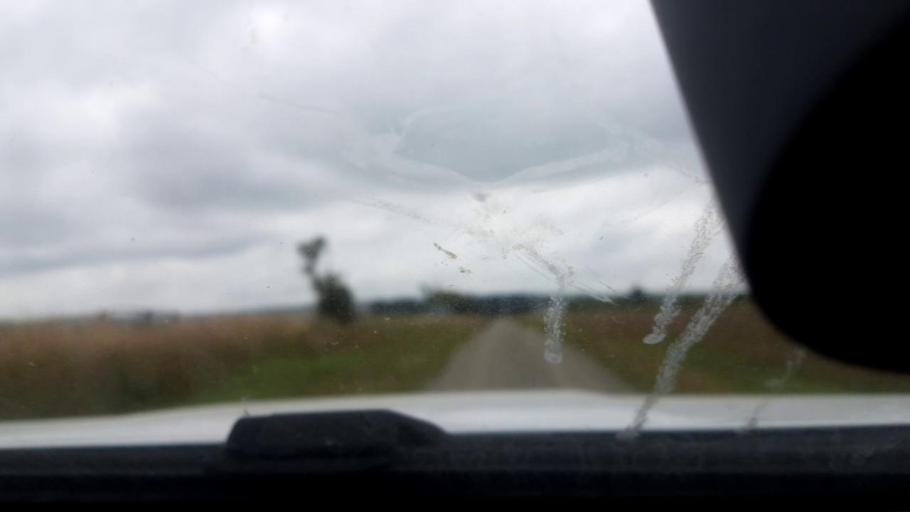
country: NZ
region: Canterbury
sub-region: Timaru District
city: Pleasant Point
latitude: -44.2282
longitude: 171.1654
